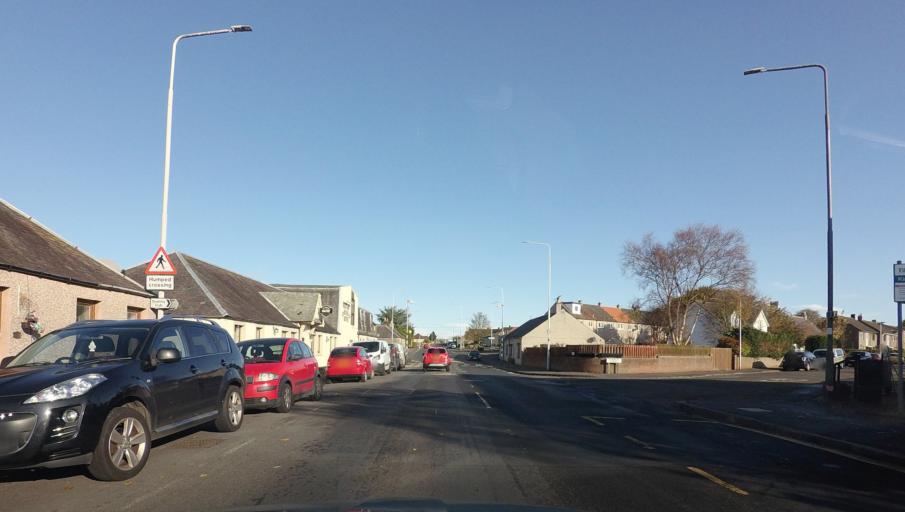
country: GB
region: Scotland
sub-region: Fife
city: Townhill
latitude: 56.0977
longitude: -3.4075
